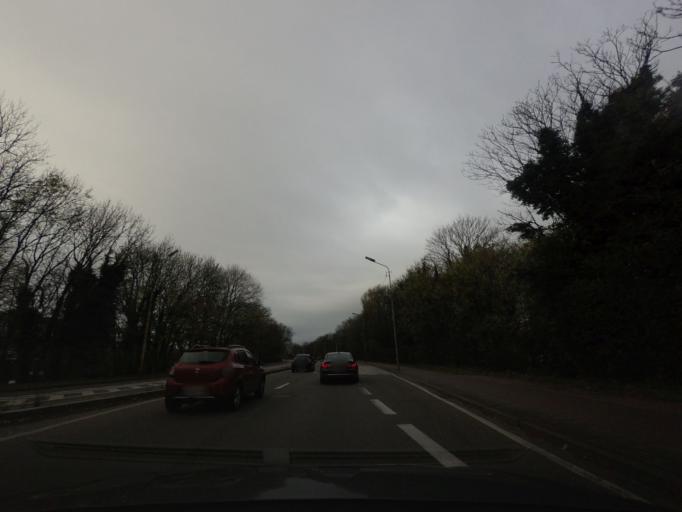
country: BE
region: Flanders
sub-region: Provincie Antwerpen
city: Antwerpen
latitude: 51.2402
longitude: 4.4354
